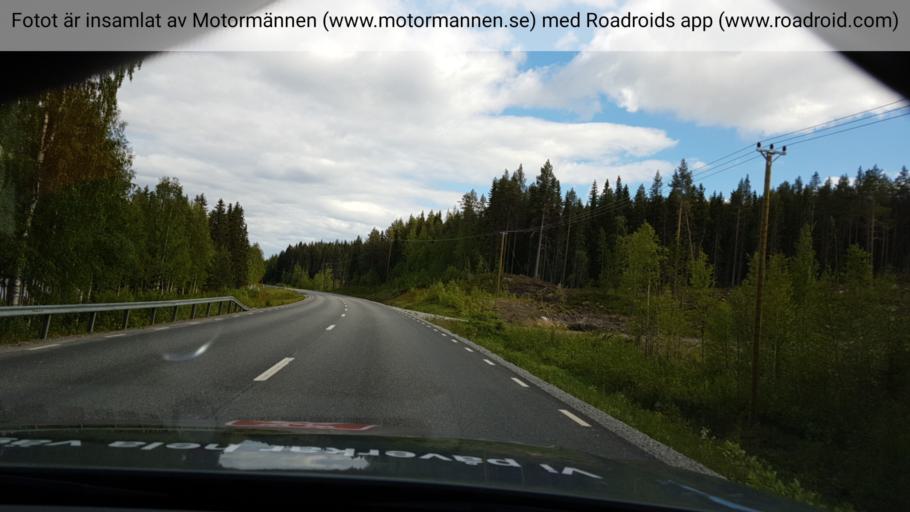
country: SE
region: Jaemtland
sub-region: Stroemsunds Kommun
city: Stroemsund
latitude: 64.1865
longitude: 15.6434
